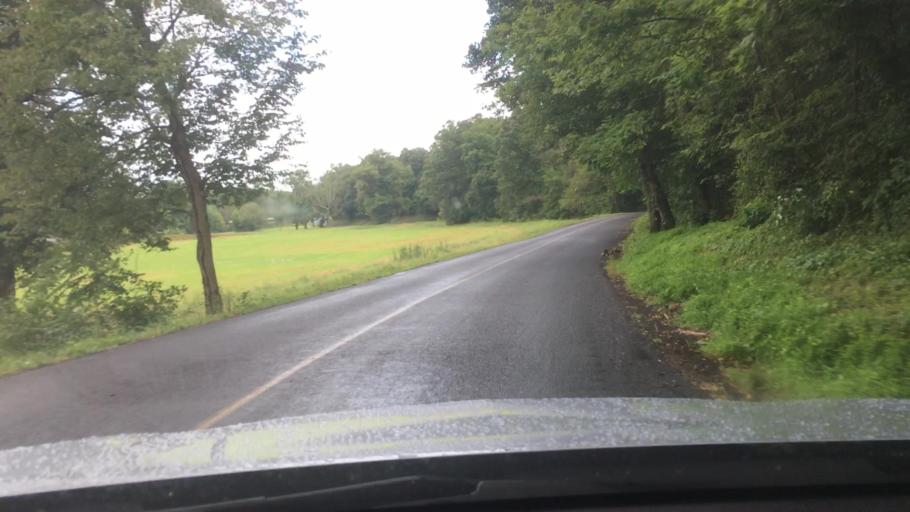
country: US
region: Pennsylvania
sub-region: Franklin County
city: Greencastle
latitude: 39.8697
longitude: -77.7884
